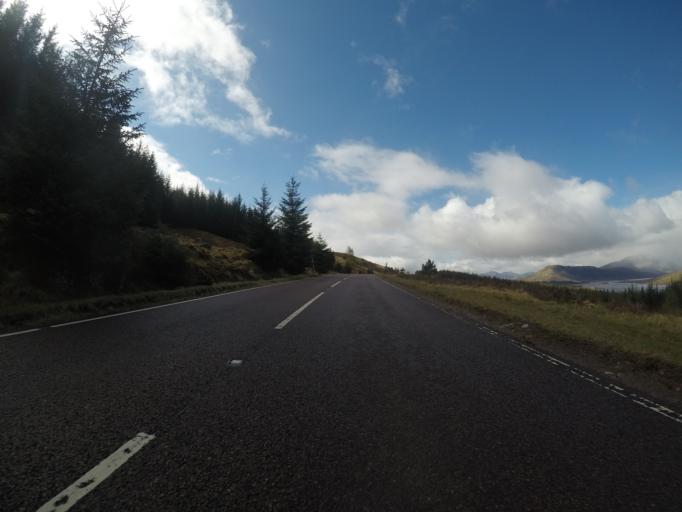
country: GB
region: Scotland
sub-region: Highland
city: Spean Bridge
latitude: 57.1044
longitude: -4.9870
